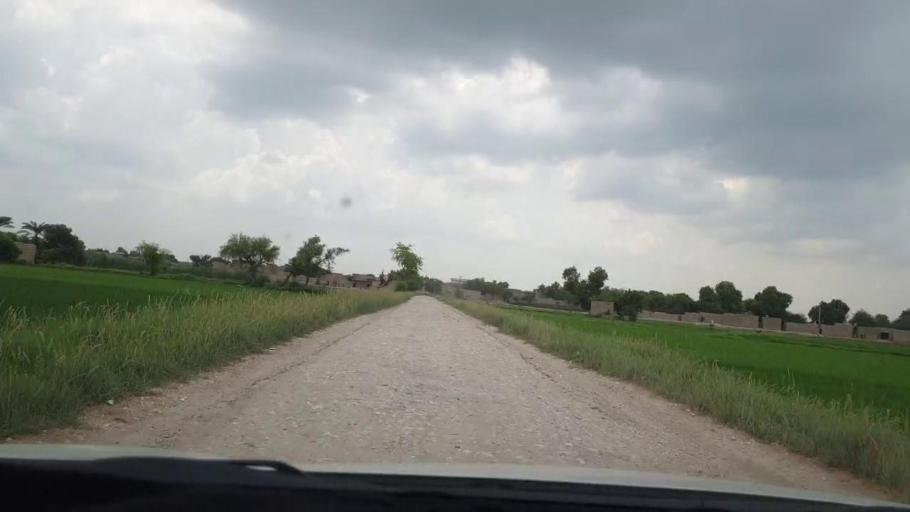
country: PK
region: Sindh
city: Dokri
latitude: 27.3286
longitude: 68.1029
